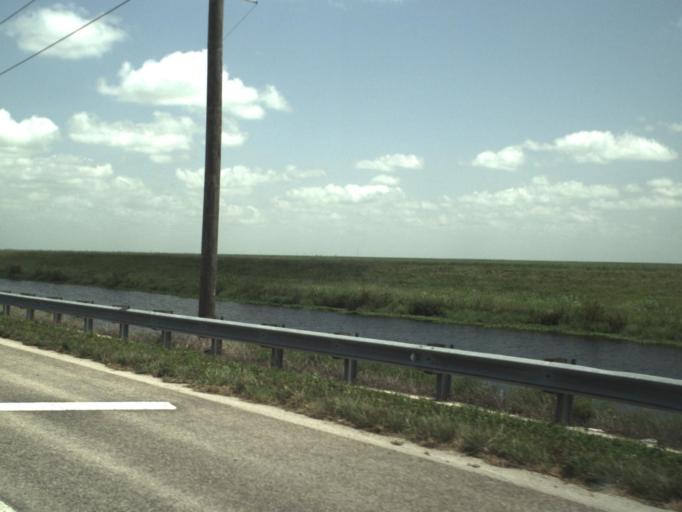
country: US
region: Florida
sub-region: Palm Beach County
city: Belle Glade Camp
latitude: 26.5831
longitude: -80.7108
